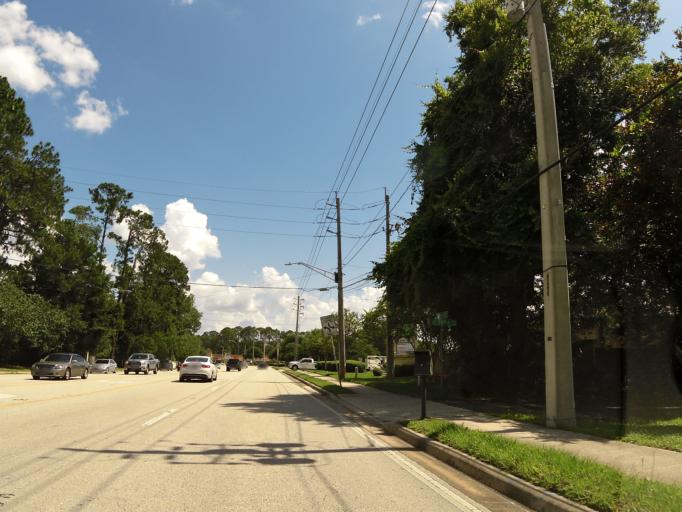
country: US
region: Florida
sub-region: Saint Johns County
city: Fruit Cove
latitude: 30.1859
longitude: -81.6080
